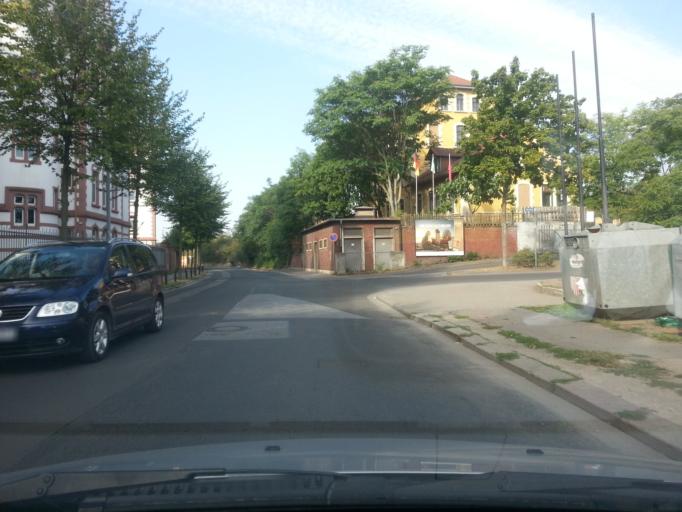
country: DE
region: Rheinland-Pfalz
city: Worms
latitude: 49.6417
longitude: 8.3616
